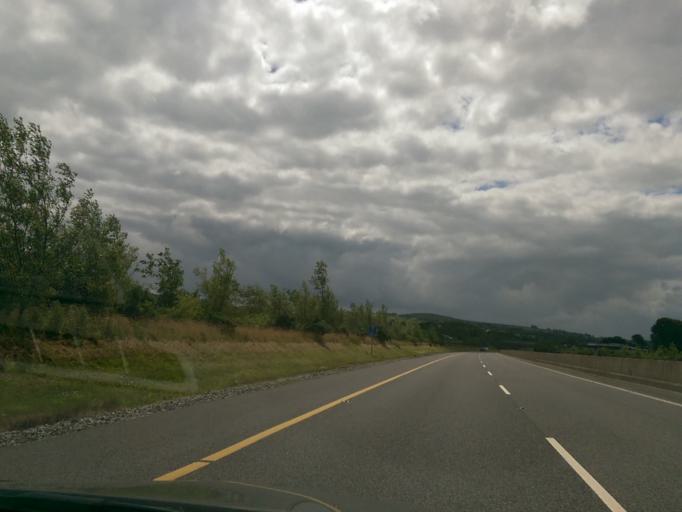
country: IE
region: Munster
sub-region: County Cork
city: Mitchelstown
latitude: 52.2612
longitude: -8.2497
